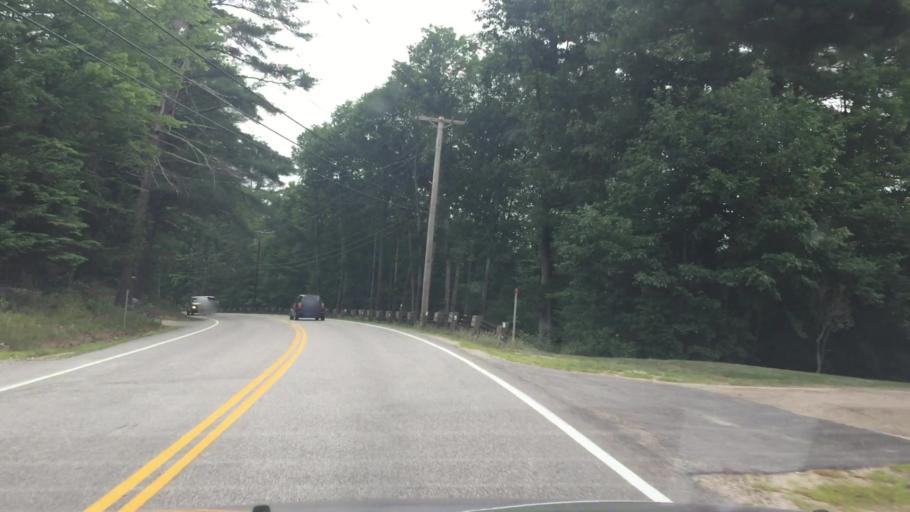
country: US
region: New Hampshire
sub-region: Carroll County
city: Moultonborough
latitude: 43.7344
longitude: -71.4151
